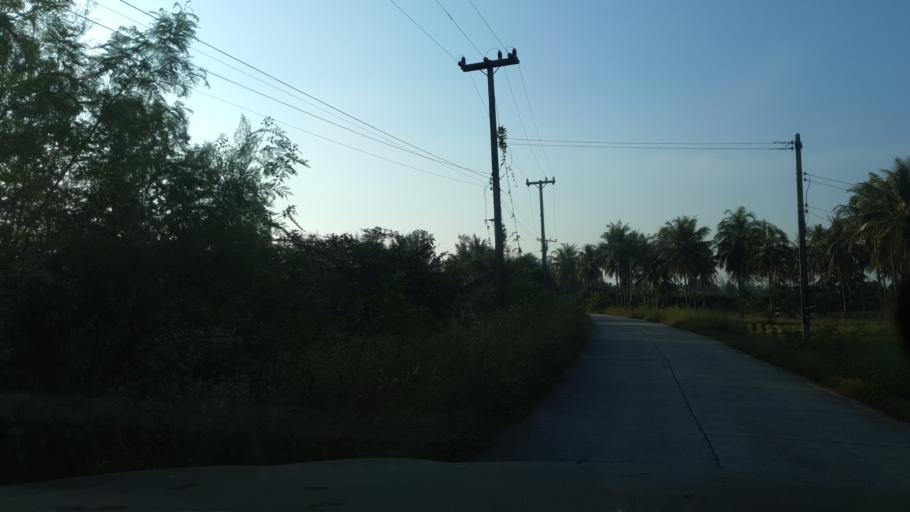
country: TH
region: Prachuap Khiri Khan
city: Bang Saphan
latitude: 11.2824
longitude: 99.5490
